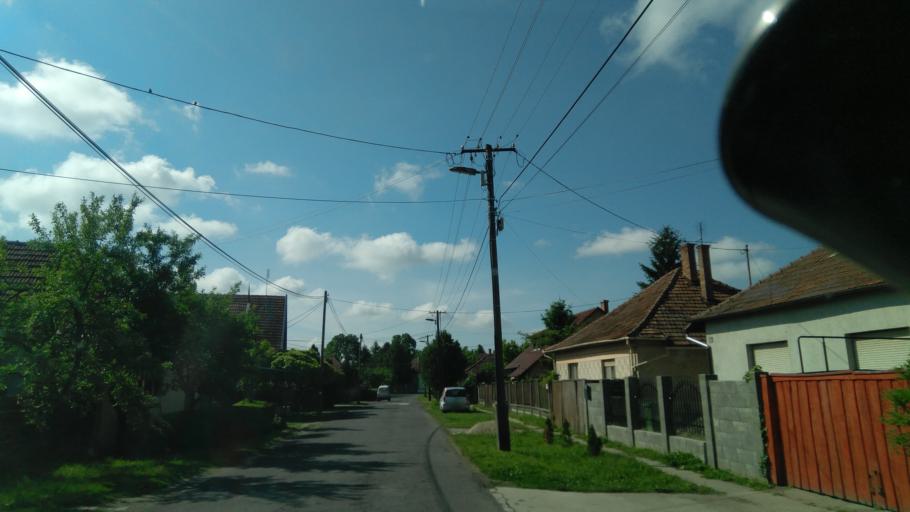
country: HU
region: Bekes
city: Bekes
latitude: 46.7807
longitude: 21.1246
